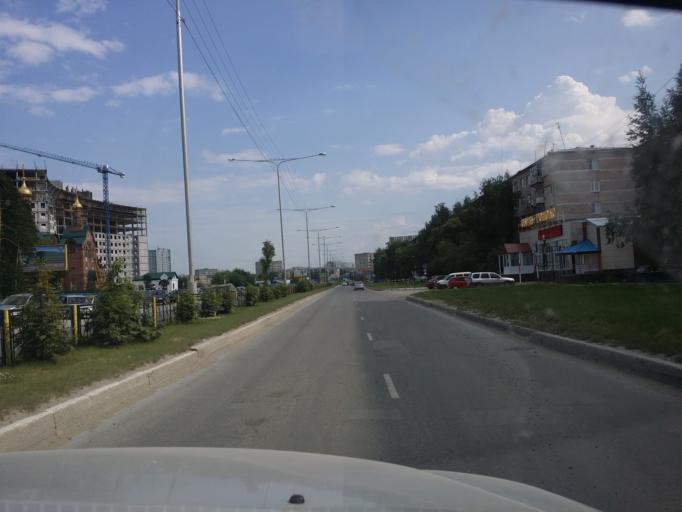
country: RU
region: Khanty-Mansiyskiy Avtonomnyy Okrug
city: Nizhnevartovsk
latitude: 60.9503
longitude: 76.5624
